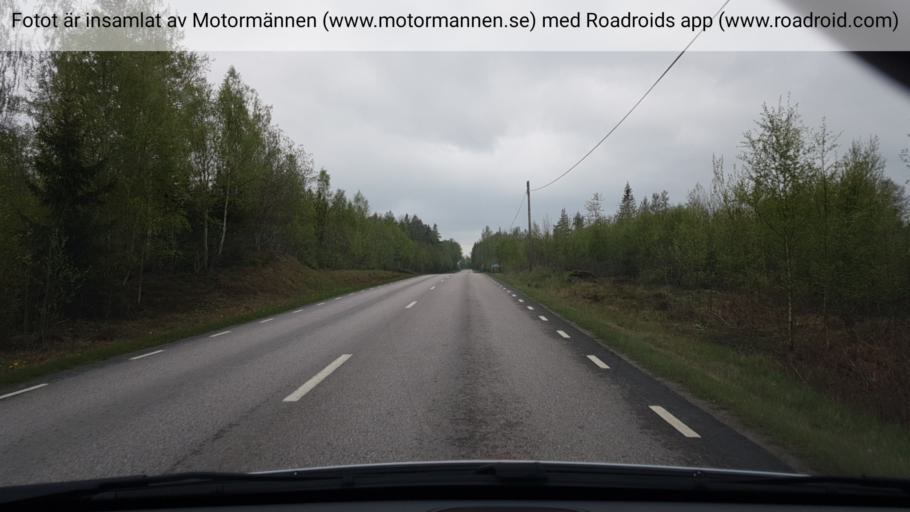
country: SE
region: Vaestra Goetaland
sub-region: Skovde Kommun
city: Stopen
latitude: 58.5256
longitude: 13.9869
